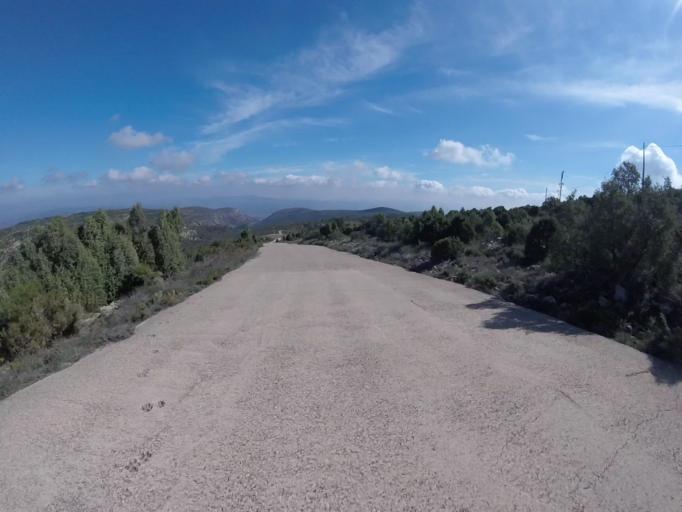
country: ES
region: Valencia
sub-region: Provincia de Castello
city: Sarratella
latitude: 40.3223
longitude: 0.0269
